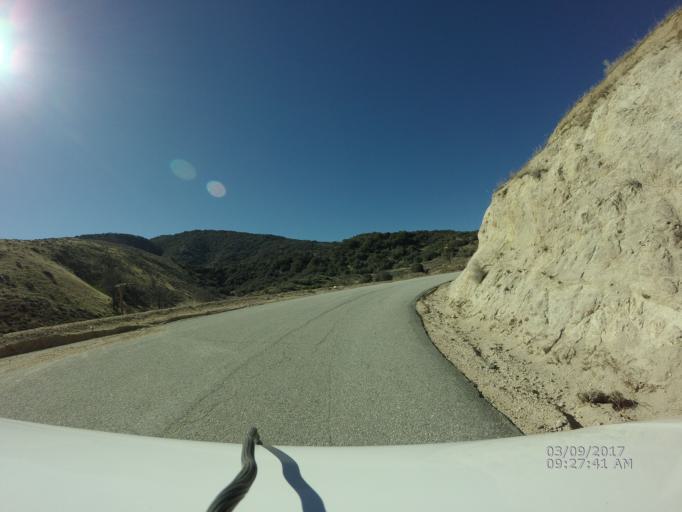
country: US
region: California
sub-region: Kern County
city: Lebec
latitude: 34.7491
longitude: -118.6979
